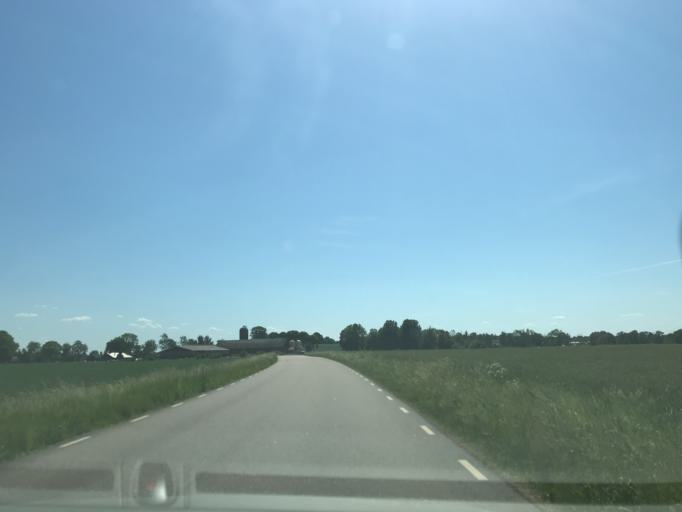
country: SE
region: Vaestra Goetaland
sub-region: Gotene Kommun
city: Kallby
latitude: 58.5182
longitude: 13.3200
